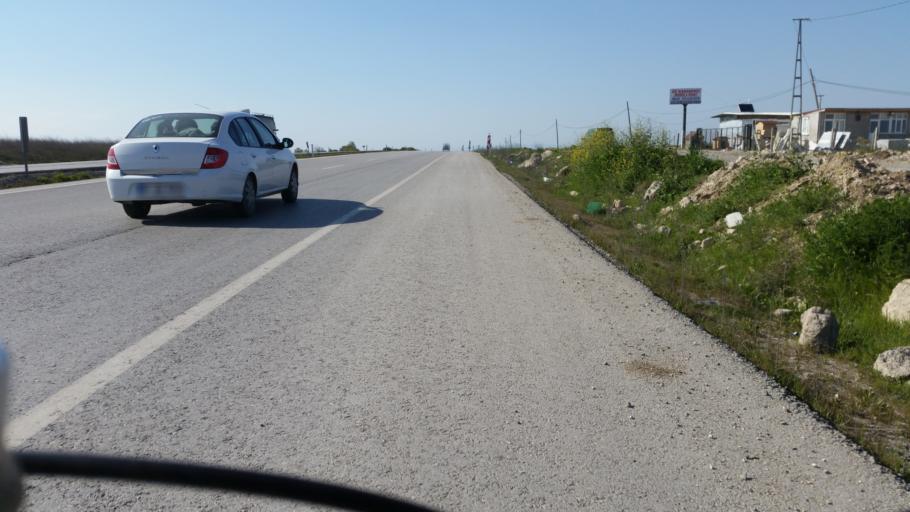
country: TR
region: Tekirdag
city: Cerkezkoey
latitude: 41.3418
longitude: 27.9645
